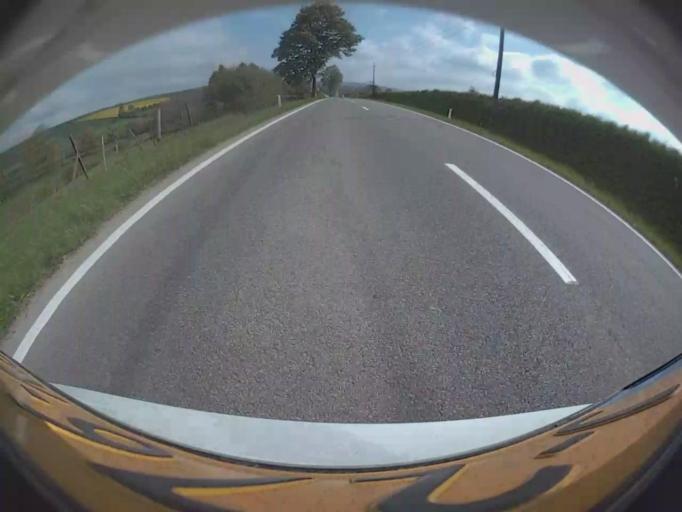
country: BE
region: Wallonia
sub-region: Province de Namur
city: Somme-Leuze
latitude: 50.3262
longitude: 5.3541
